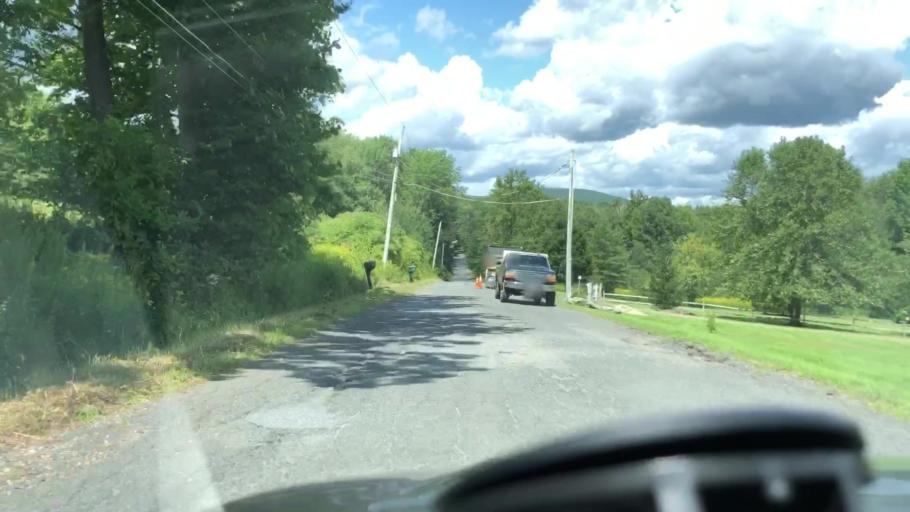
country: US
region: Massachusetts
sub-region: Berkshire County
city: North Adams
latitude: 42.6747
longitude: -73.1390
